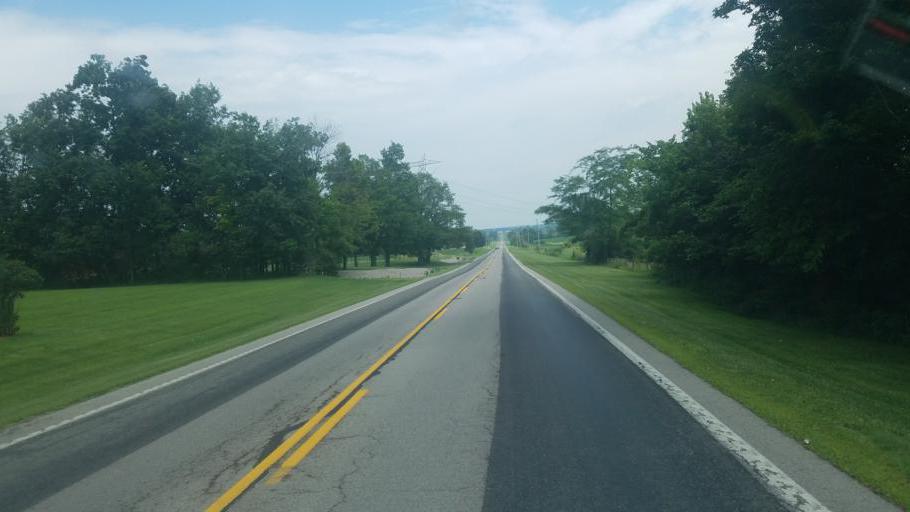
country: US
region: Ohio
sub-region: Logan County
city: Northwood
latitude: 40.4082
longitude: -83.6288
